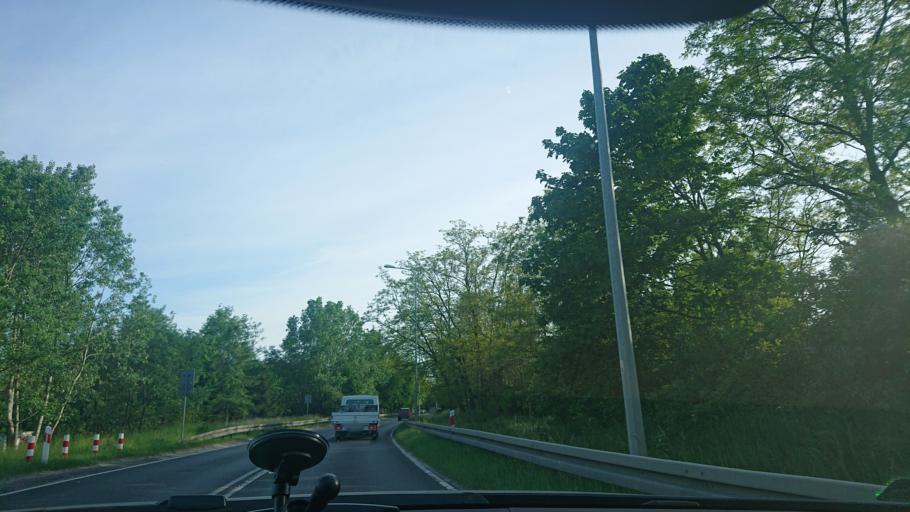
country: PL
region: Greater Poland Voivodeship
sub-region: Powiat gnieznienski
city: Gniezno
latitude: 52.5239
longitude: 17.5855
